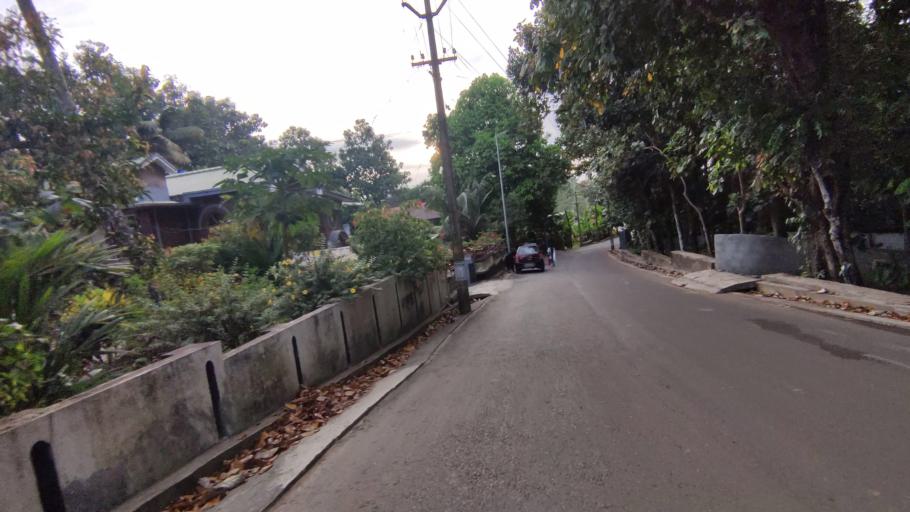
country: IN
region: Kerala
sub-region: Kottayam
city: Kottayam
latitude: 9.6433
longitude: 76.5171
